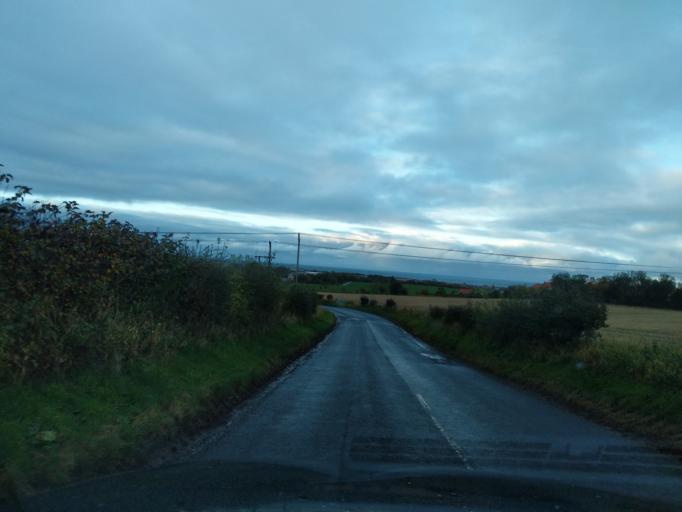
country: GB
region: Scotland
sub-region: East Lothian
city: Dunbar
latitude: 55.9820
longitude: -2.5174
